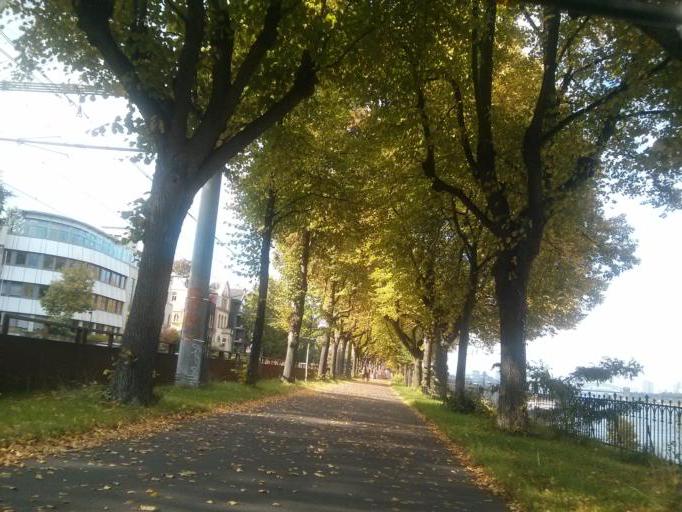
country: DE
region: North Rhine-Westphalia
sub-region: Regierungsbezirk Koln
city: Poll
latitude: 50.9049
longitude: 6.9799
